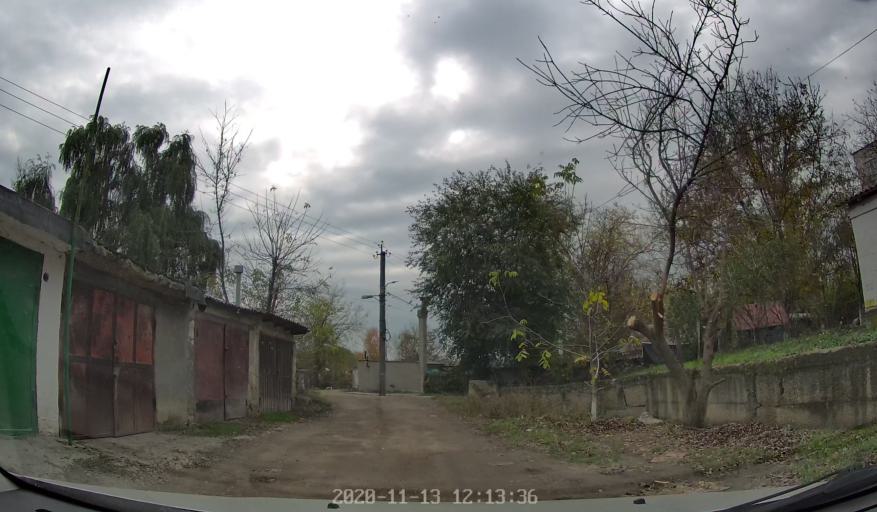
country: MD
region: Chisinau
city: Chisinau
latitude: 46.9540
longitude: 28.8381
